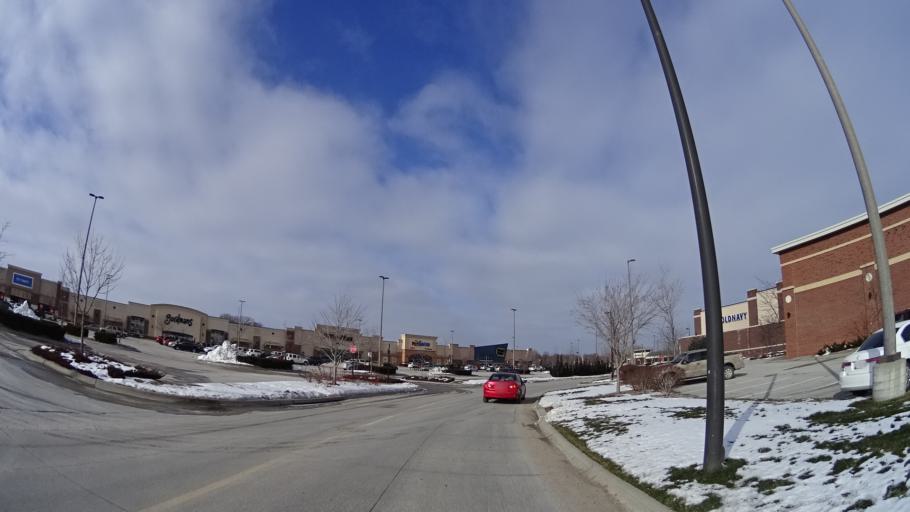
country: US
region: Nebraska
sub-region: Sarpy County
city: Papillion
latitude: 41.1348
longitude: -96.0296
